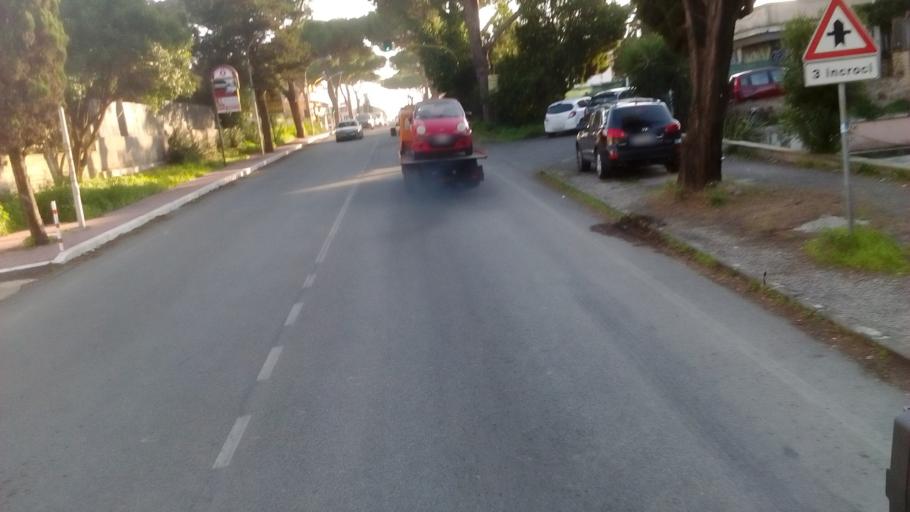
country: IT
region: Latium
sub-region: Citta metropolitana di Roma Capitale
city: Marino
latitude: 41.7620
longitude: 12.6161
